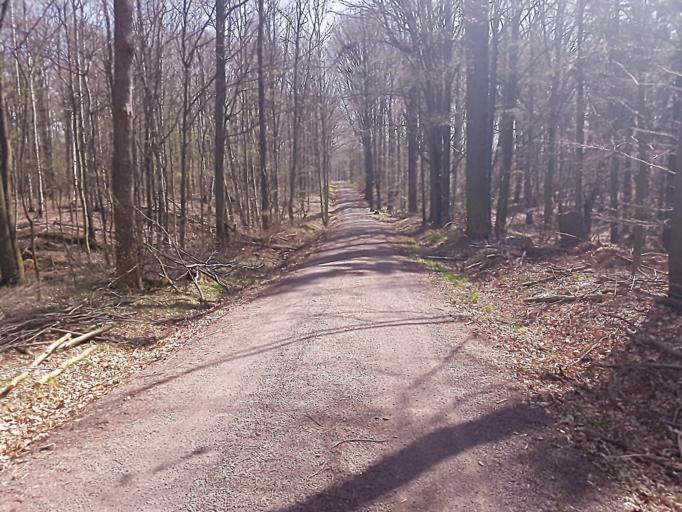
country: DE
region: Saxony
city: Leisnig
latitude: 51.1499
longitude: 12.9749
